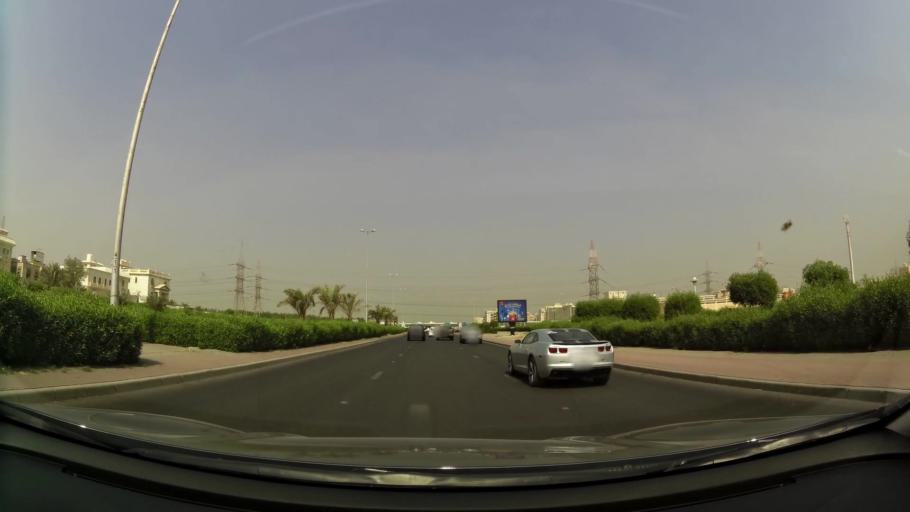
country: KW
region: Al Asimah
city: Ar Rabiyah
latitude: 29.2951
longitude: 47.9059
